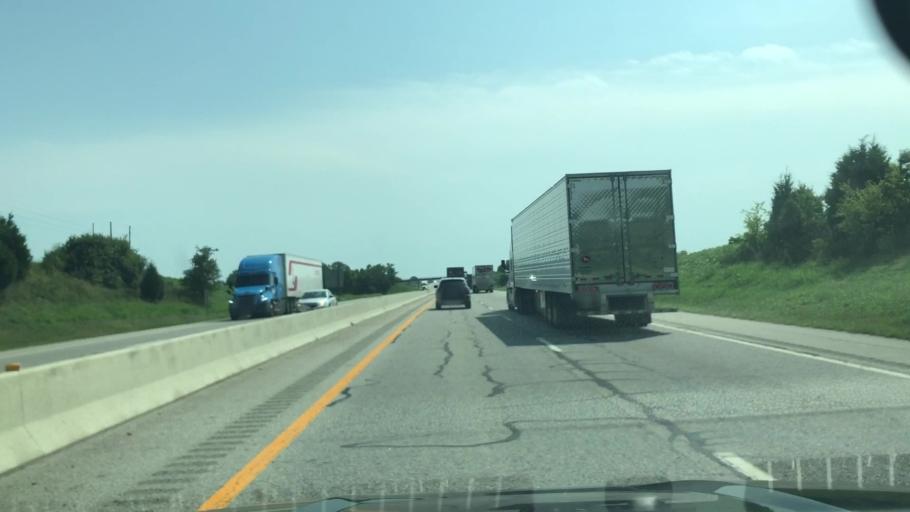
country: US
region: Oklahoma
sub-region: Ottawa County
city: Miami
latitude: 36.8338
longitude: -94.8649
